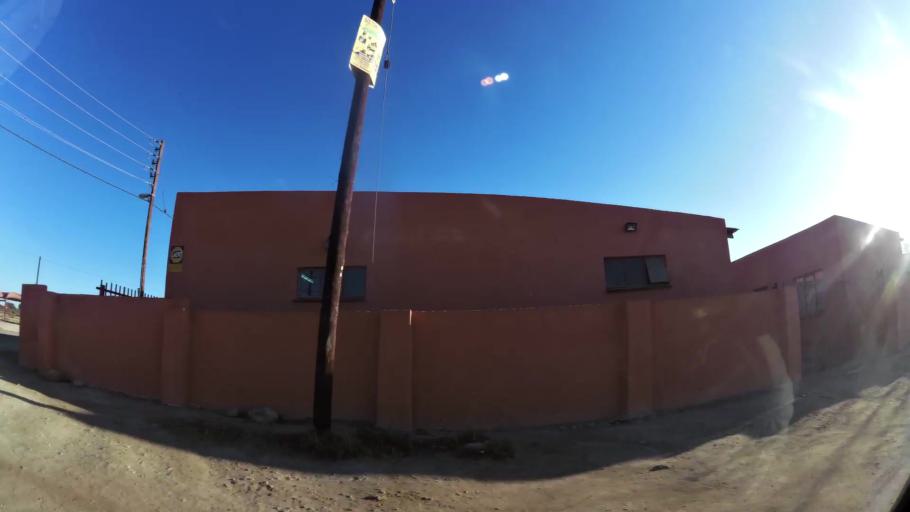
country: ZA
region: Limpopo
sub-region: Capricorn District Municipality
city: Polokwane
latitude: -23.8415
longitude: 29.3527
